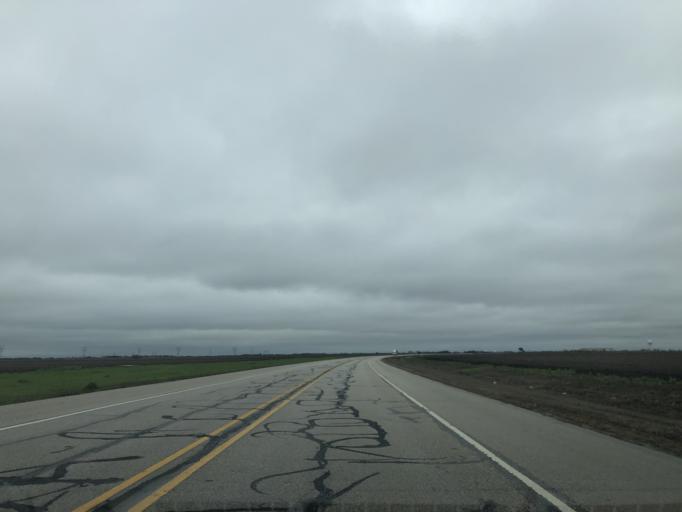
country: US
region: Texas
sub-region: Williamson County
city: Hutto
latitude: 30.5989
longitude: -97.5323
